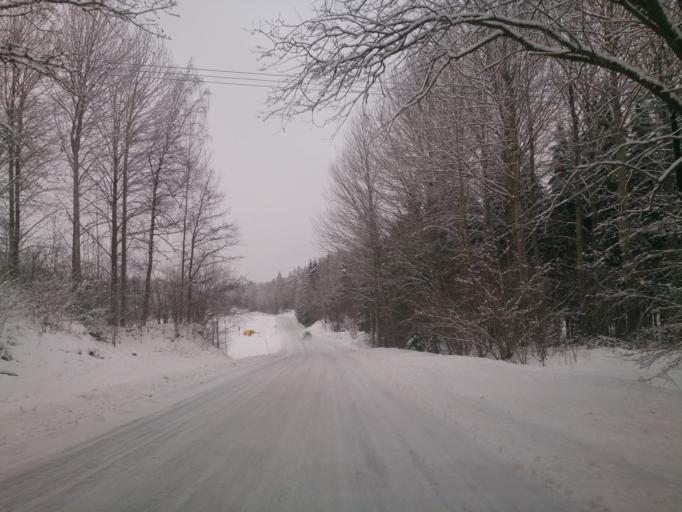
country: SE
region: OEstergoetland
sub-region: Atvidabergs Kommun
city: Atvidaberg
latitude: 58.3136
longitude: 16.0256
